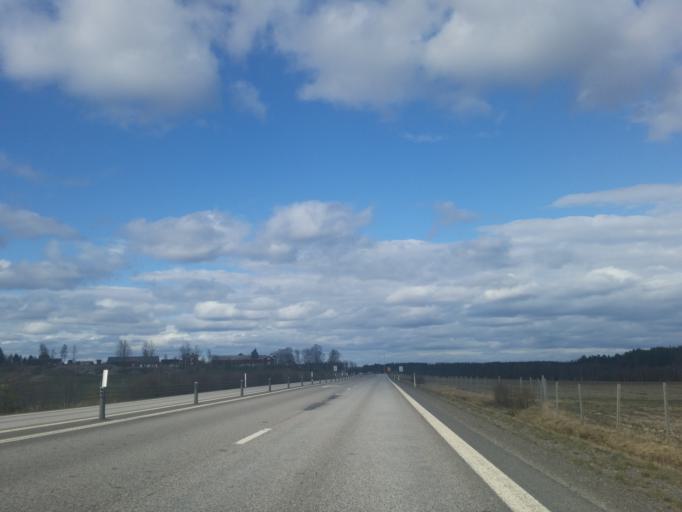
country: SE
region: Vaesterbotten
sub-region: Robertsfors Kommun
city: Robertsfors
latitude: 64.0744
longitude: 20.8600
